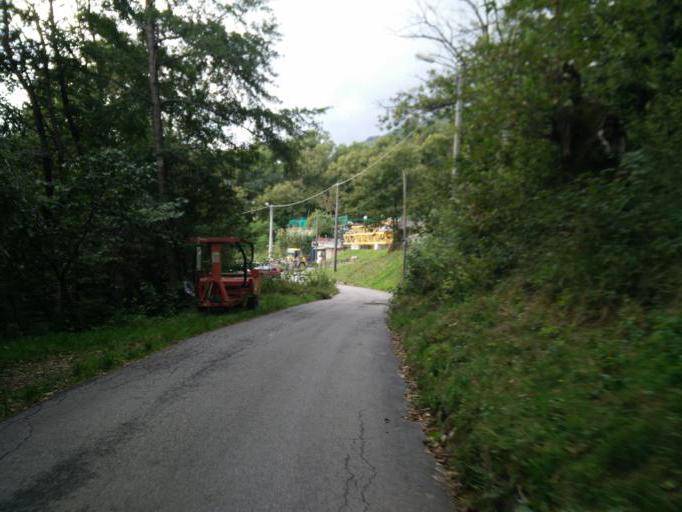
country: IT
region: Lombardy
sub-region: Provincia di Como
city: Livo
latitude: 46.1708
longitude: 9.3066
